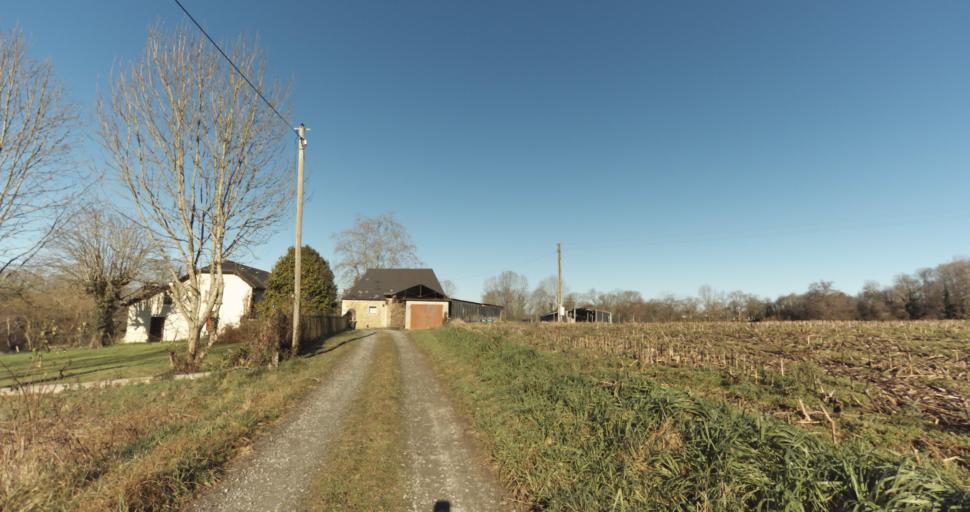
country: FR
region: Aquitaine
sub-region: Departement des Pyrenees-Atlantiques
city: Morlaas
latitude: 43.3459
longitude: -0.2468
